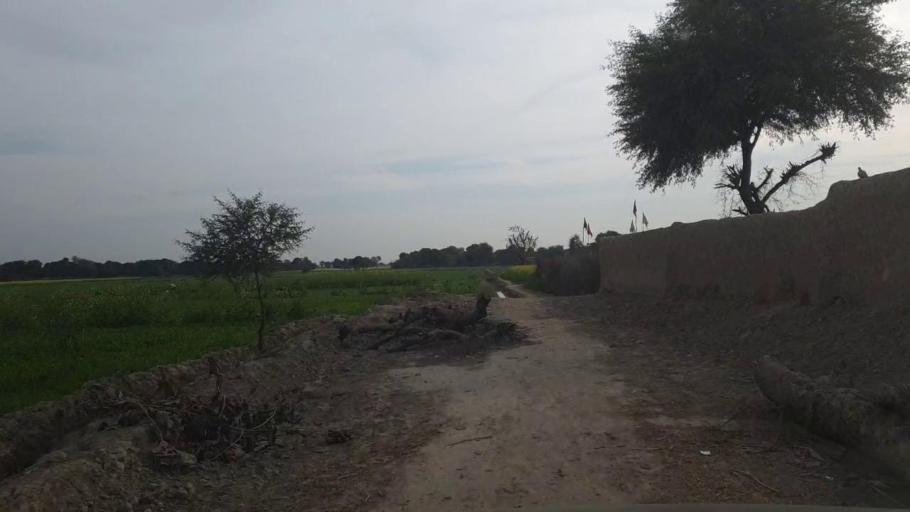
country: PK
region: Sindh
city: Shahpur Chakar
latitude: 26.1103
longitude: 68.5278
